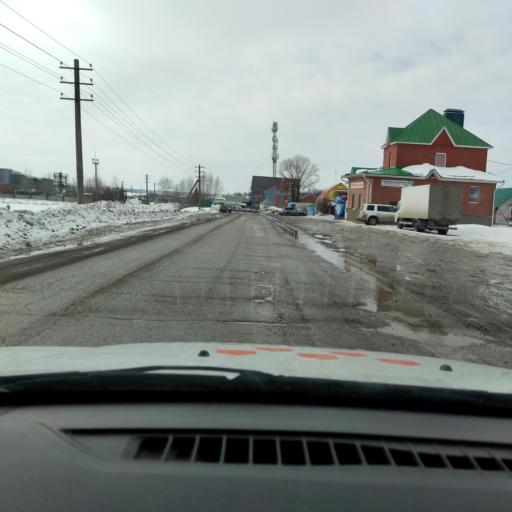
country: RU
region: Bashkortostan
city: Mikhaylovka
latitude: 54.8383
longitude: 55.8298
